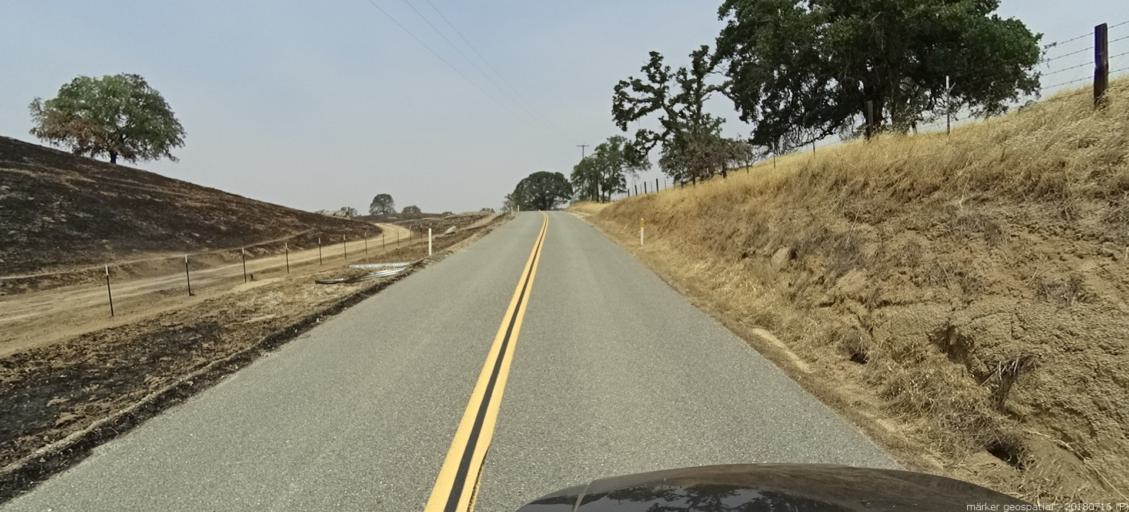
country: US
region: California
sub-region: Madera County
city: Yosemite Lakes
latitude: 37.1435
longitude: -119.9088
